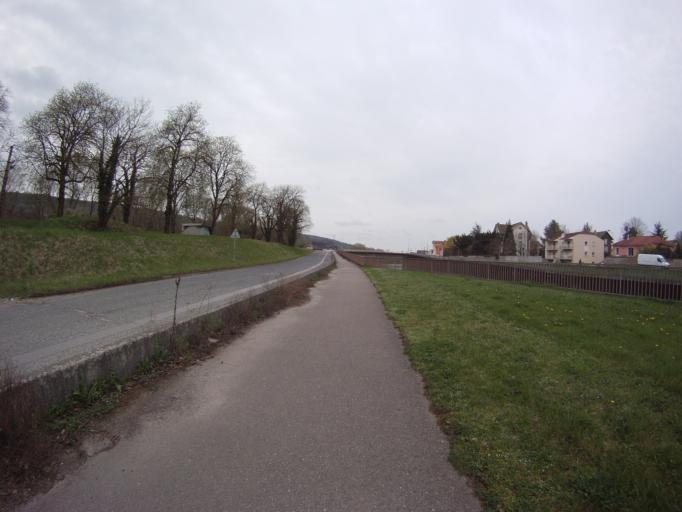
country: FR
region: Lorraine
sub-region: Departement de Meurthe-et-Moselle
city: Pont-Saint-Vincent
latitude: 48.6072
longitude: 6.1029
